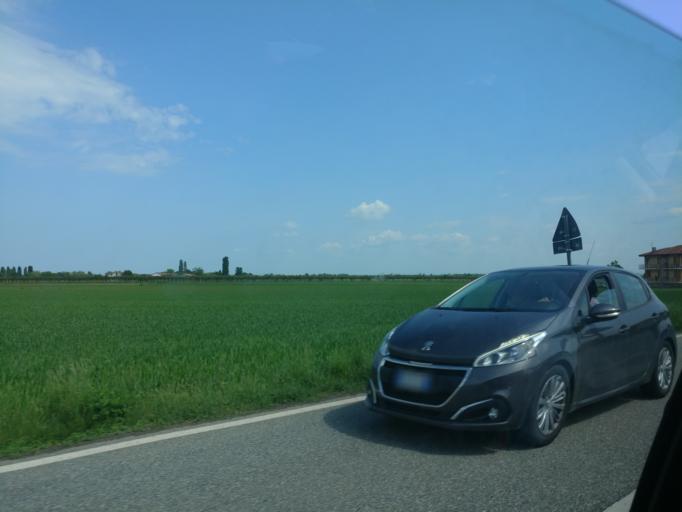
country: IT
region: Piedmont
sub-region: Provincia di Torino
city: Cavour
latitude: 44.7754
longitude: 7.3877
